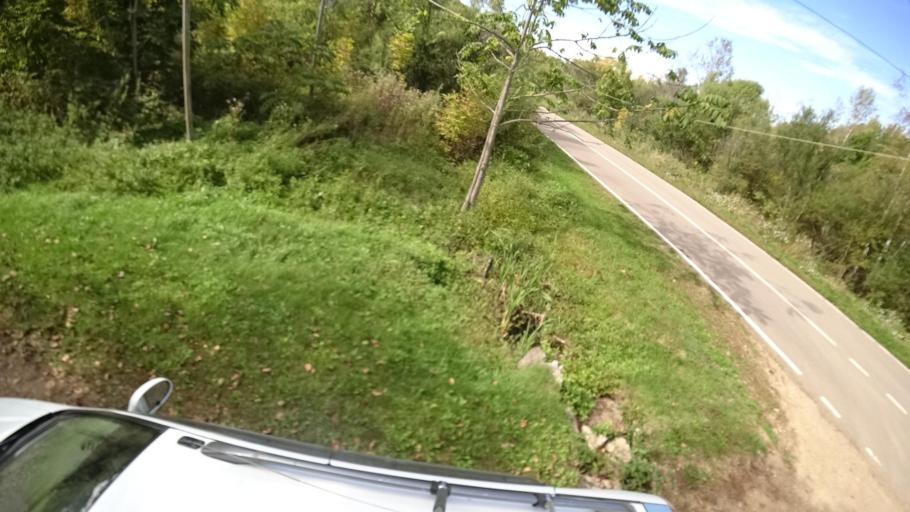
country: RU
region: Primorskiy
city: Yakovlevka
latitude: 44.3940
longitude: 133.6064
